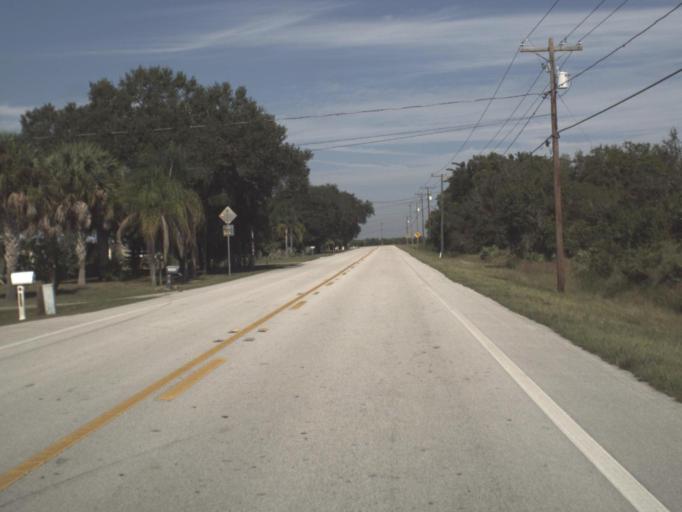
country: US
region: Florida
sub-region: Highlands County
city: Avon Park
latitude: 27.5650
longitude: -81.4546
